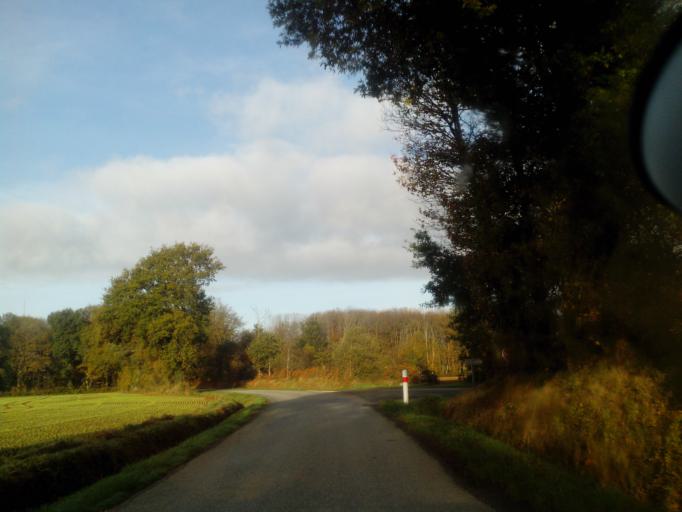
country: FR
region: Brittany
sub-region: Departement du Morbihan
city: Meneac
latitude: 48.1248
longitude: -2.4367
